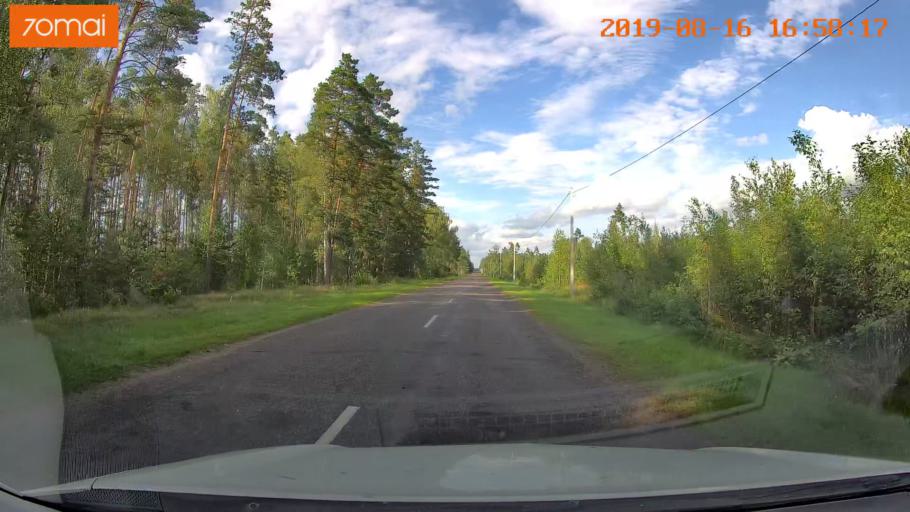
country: BY
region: Mogilev
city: Hlusha
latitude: 53.2672
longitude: 28.8319
